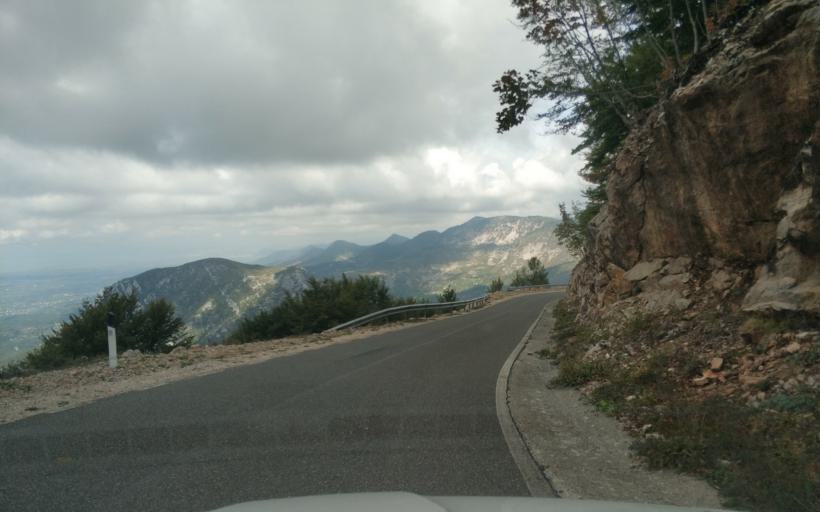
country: AL
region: Durres
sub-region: Rrethi i Krujes
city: Kruje
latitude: 41.5214
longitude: 19.8049
